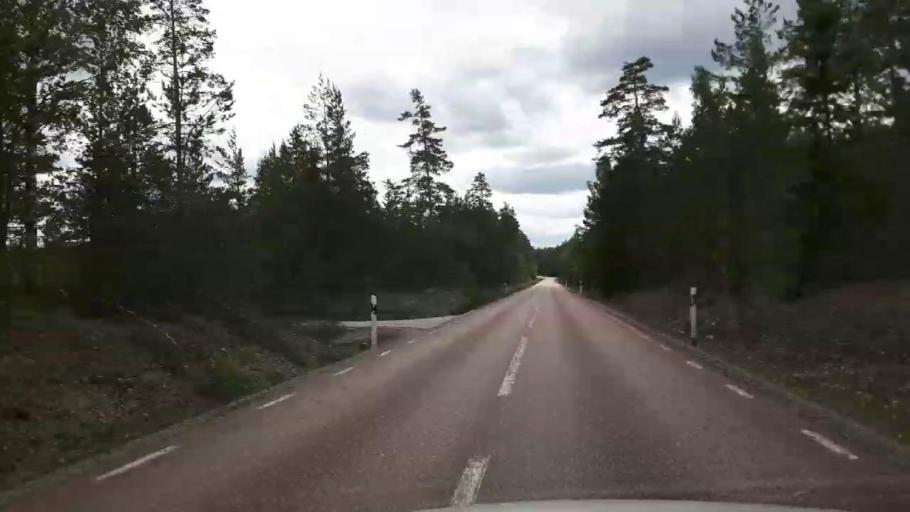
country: SE
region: Vaestmanland
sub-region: Fagersta Kommun
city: Fagersta
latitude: 59.8674
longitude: 15.8422
